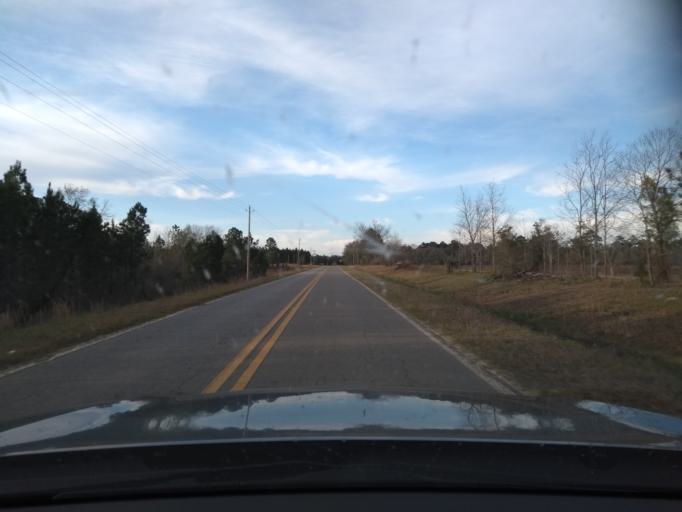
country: US
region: Georgia
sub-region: Evans County
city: Claxton
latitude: 32.2297
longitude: -81.7706
